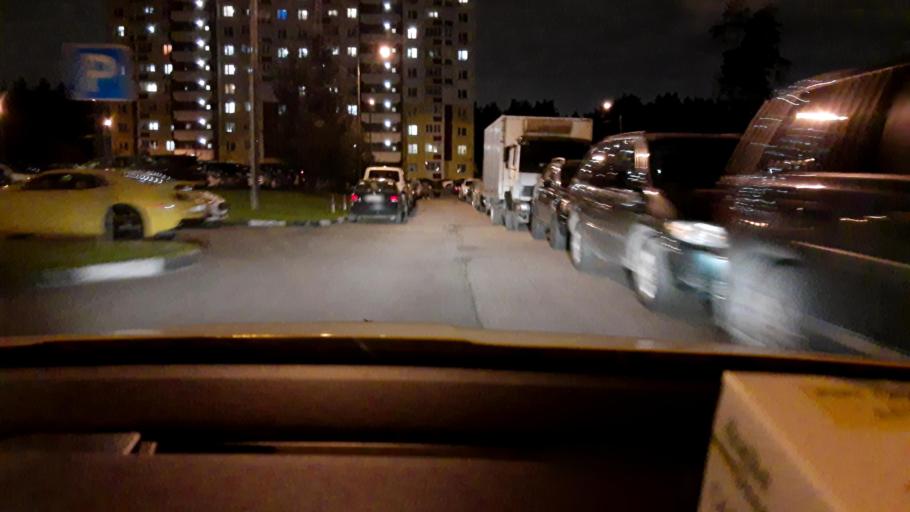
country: RU
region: Moskovskaya
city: Reutov
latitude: 55.7391
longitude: 37.8823
